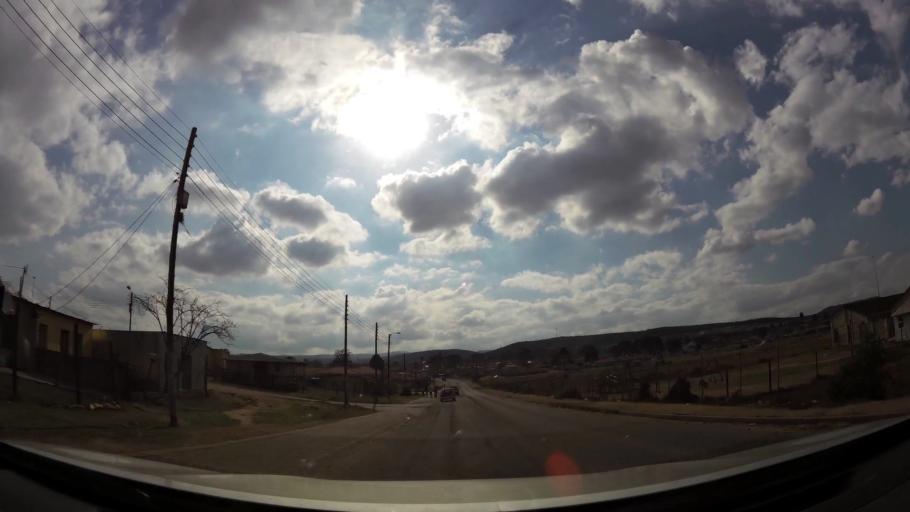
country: ZA
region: Eastern Cape
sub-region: Nelson Mandela Bay Metropolitan Municipality
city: Uitenhage
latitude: -33.7436
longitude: 25.3867
